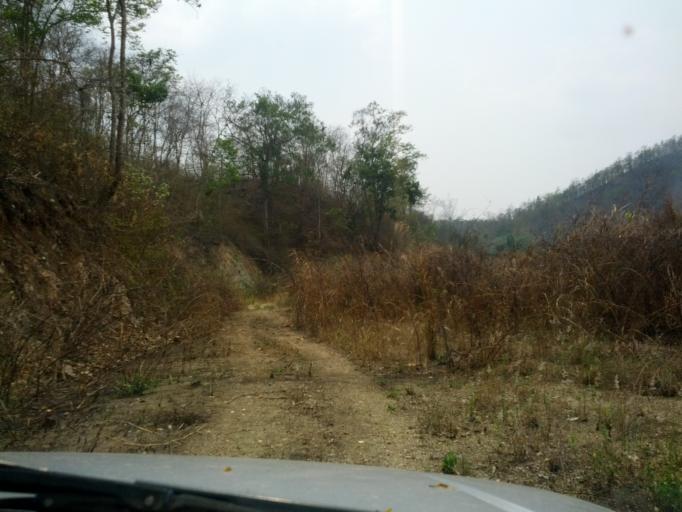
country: TH
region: Chiang Mai
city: Mae Taeng
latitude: 19.1076
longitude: 98.9818
